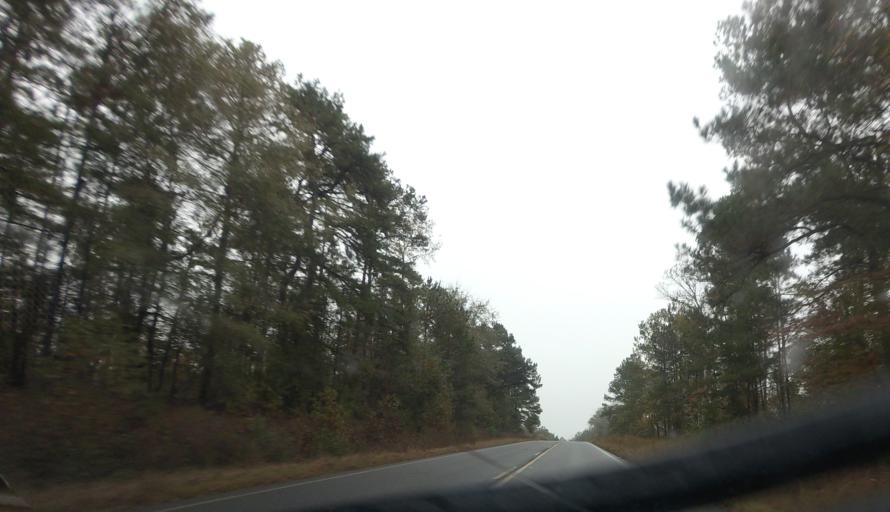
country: US
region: Georgia
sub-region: Marion County
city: Buena Vista
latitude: 32.3416
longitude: -84.4894
